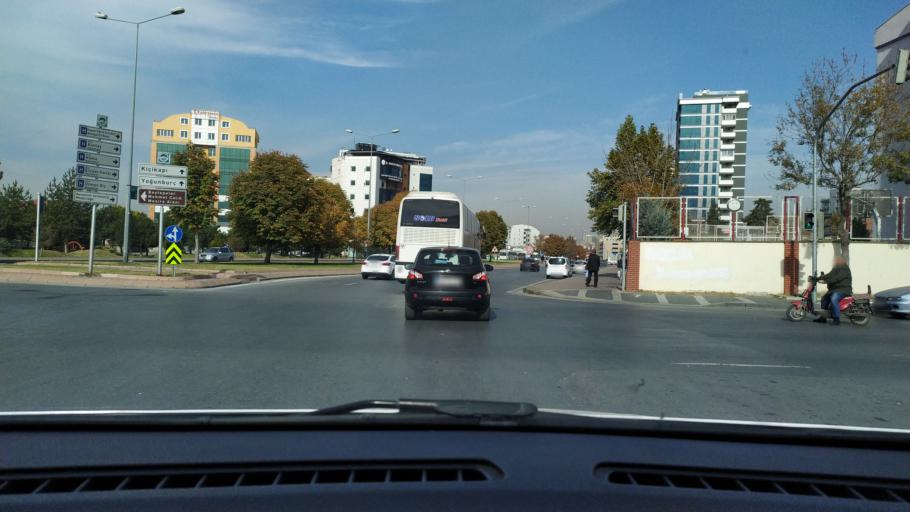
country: TR
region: Kayseri
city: Kayseri
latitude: 38.7110
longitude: 35.4911
